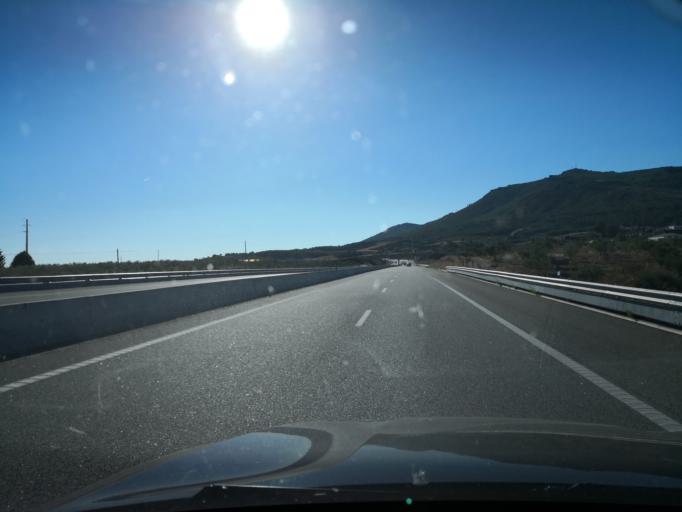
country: PT
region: Braganca
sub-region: Mirandela
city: Mirandela
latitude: 41.4630
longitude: -7.2512
